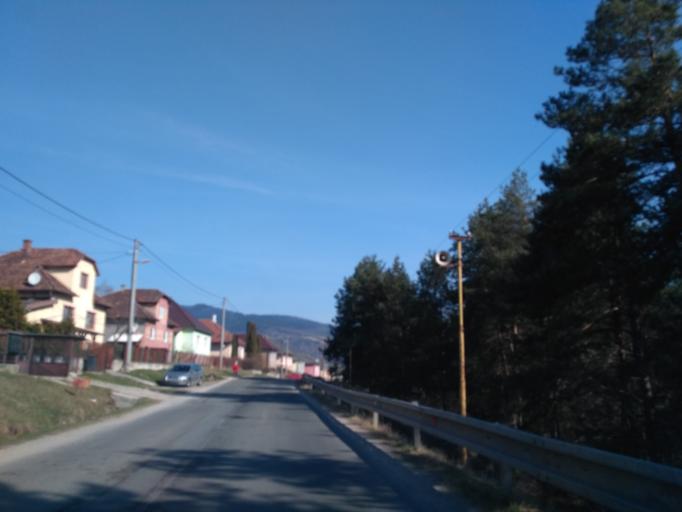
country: SK
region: Kosicky
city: Medzev
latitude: 48.7953
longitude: 20.8068
